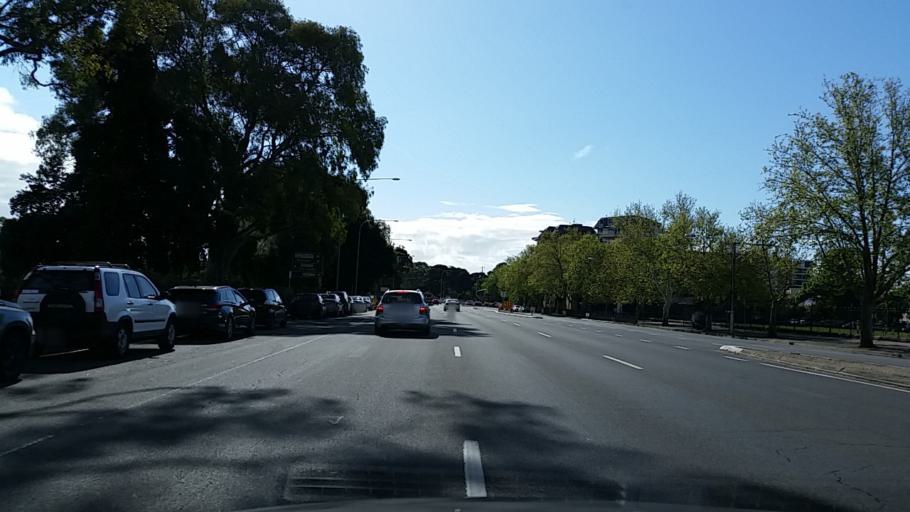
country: AU
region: South Australia
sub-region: Adelaide
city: Adelaide
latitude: -34.9241
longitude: 138.6178
